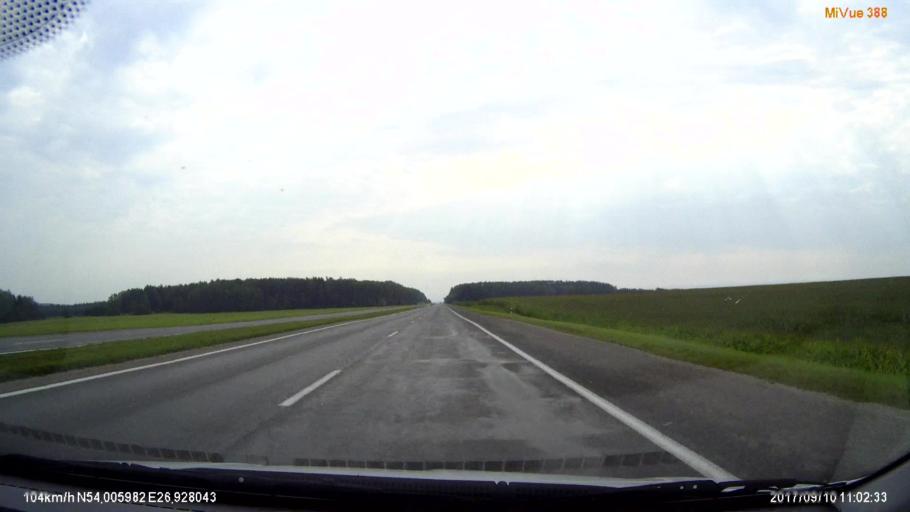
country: BY
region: Minsk
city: Rakaw
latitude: 54.0060
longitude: 26.9280
